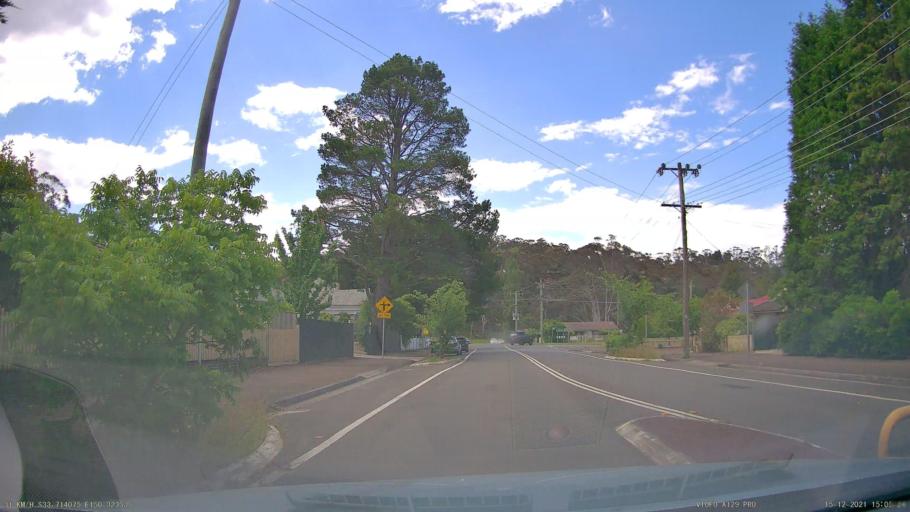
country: AU
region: New South Wales
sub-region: Blue Mountains Municipality
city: Leura
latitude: -33.7140
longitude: 150.3235
